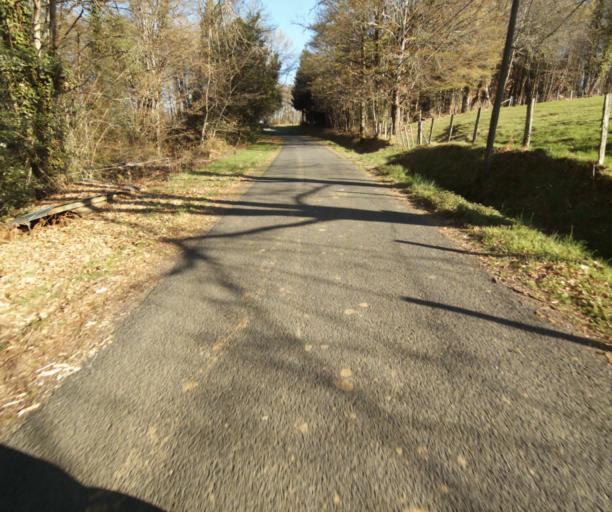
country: FR
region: Limousin
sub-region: Departement de la Correze
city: Seilhac
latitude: 45.3685
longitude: 1.7530
